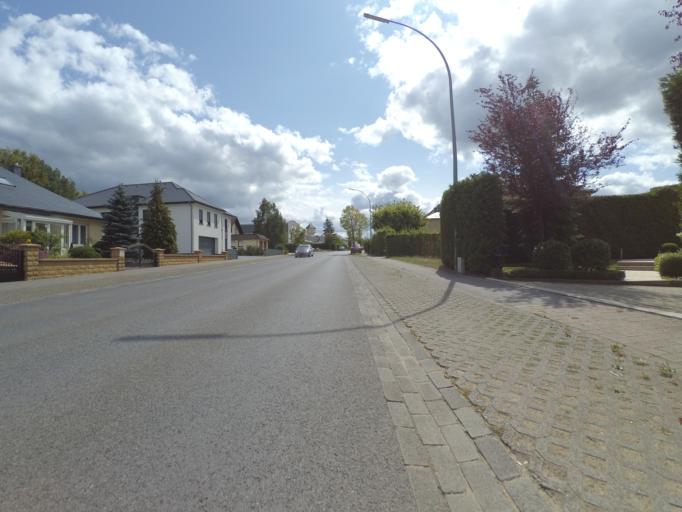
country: LU
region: Luxembourg
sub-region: Canton de Luxembourg
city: Niederanven
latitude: 49.6543
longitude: 6.2248
